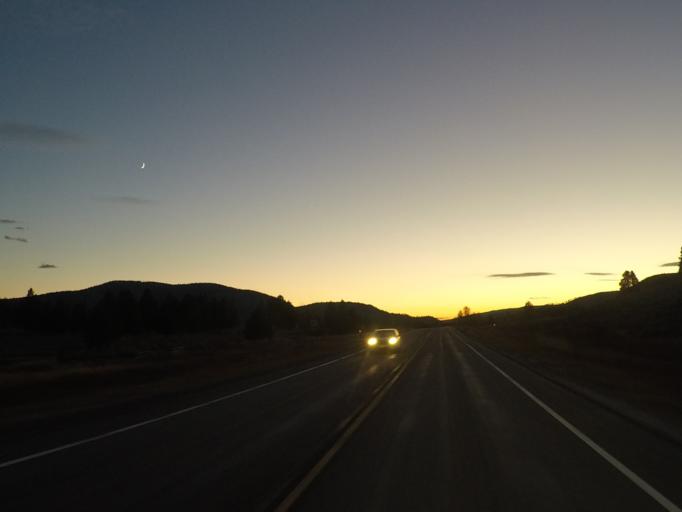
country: US
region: Montana
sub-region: Missoula County
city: Seeley Lake
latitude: 47.0415
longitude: -113.2191
